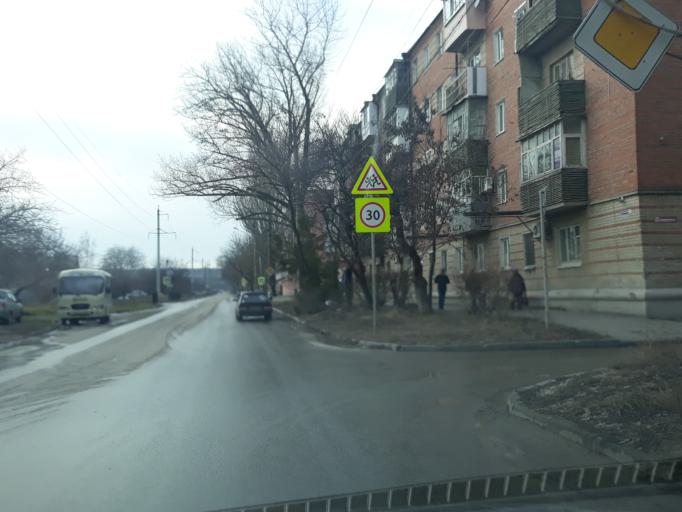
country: RU
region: Rostov
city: Taganrog
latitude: 47.2499
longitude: 38.9128
